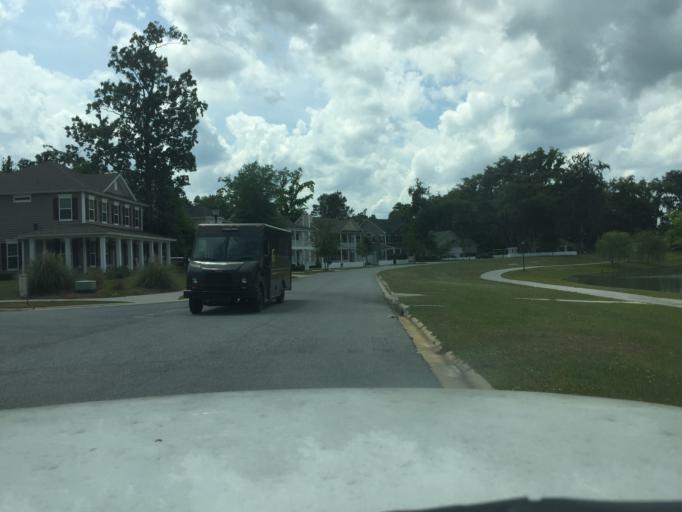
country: US
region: Georgia
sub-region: Chatham County
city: Georgetown
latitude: 32.0436
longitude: -81.2332
